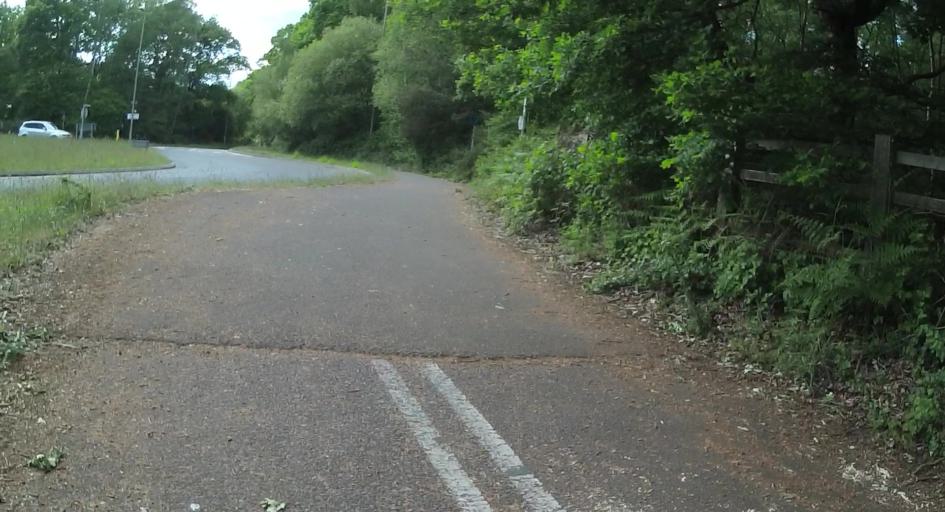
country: GB
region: England
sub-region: Hampshire
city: Fleet
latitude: 51.2838
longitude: -0.7951
